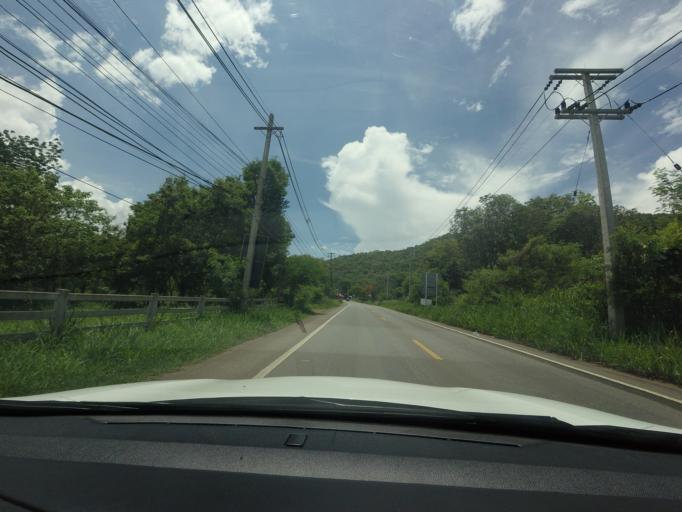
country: TH
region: Sara Buri
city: Muak Lek
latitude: 14.6198
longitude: 101.2123
